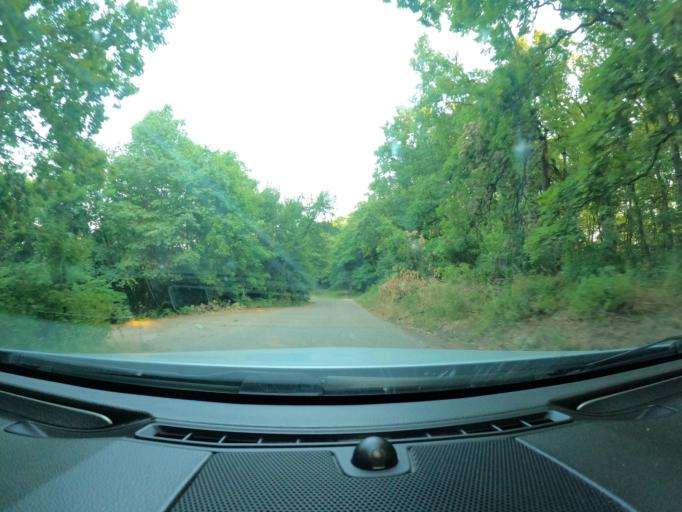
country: RS
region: Autonomna Pokrajina Vojvodina
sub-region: Juznobacki Okrug
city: Beocin
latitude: 45.1572
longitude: 19.7425
